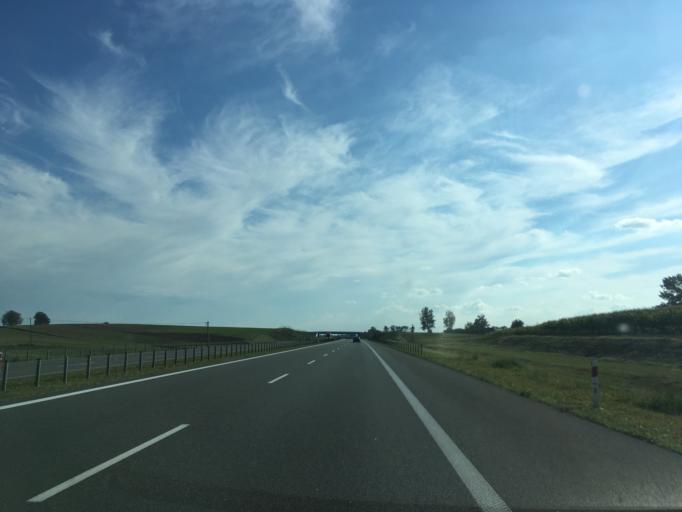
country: PL
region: Kujawsko-Pomorskie
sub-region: Powiat chelminski
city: Lisewo
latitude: 53.3147
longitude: 18.7060
